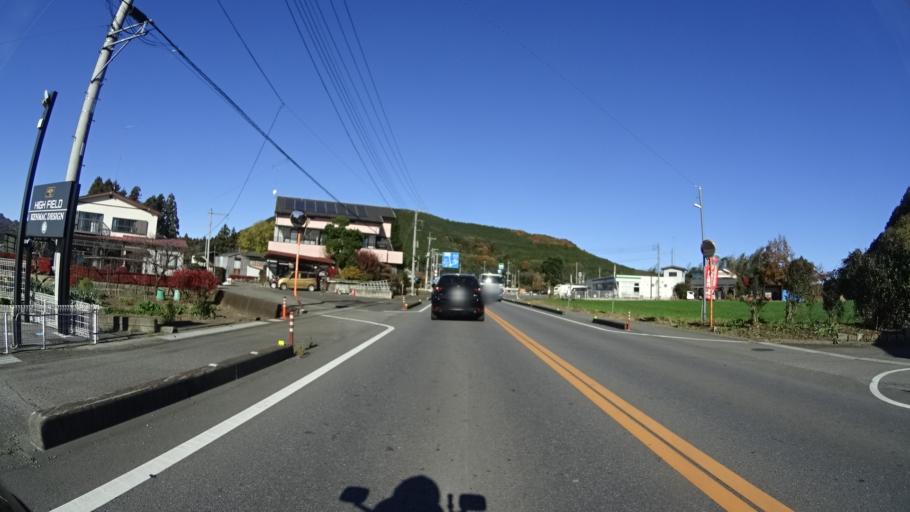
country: JP
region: Tochigi
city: Kanuma
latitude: 36.5945
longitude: 139.7993
